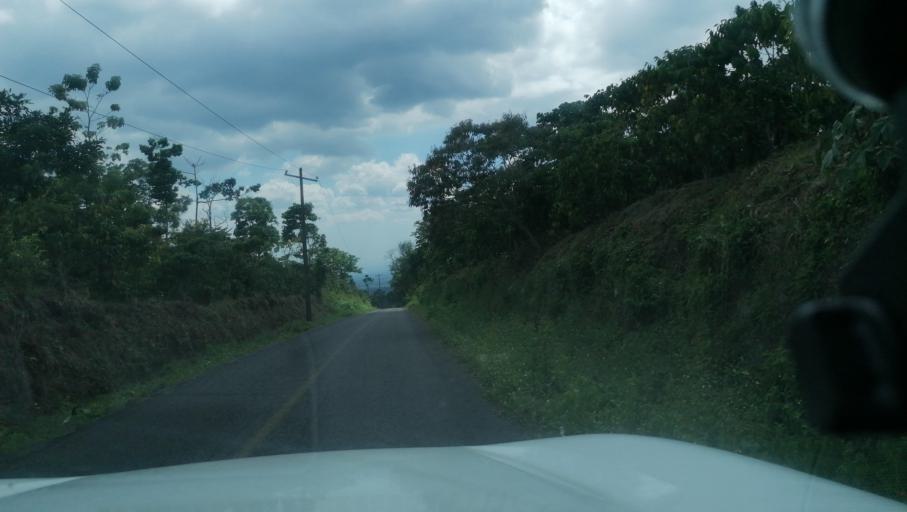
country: MX
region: Chiapas
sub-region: Cacahoatan
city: Benito Juarez
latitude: 15.0545
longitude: -92.1517
